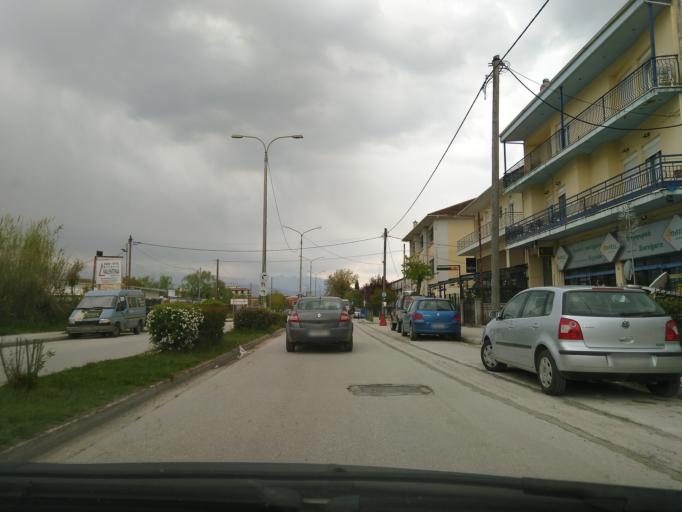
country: GR
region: Epirus
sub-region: Nomos Ioanninon
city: Ioannina
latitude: 39.6723
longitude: 20.8512
